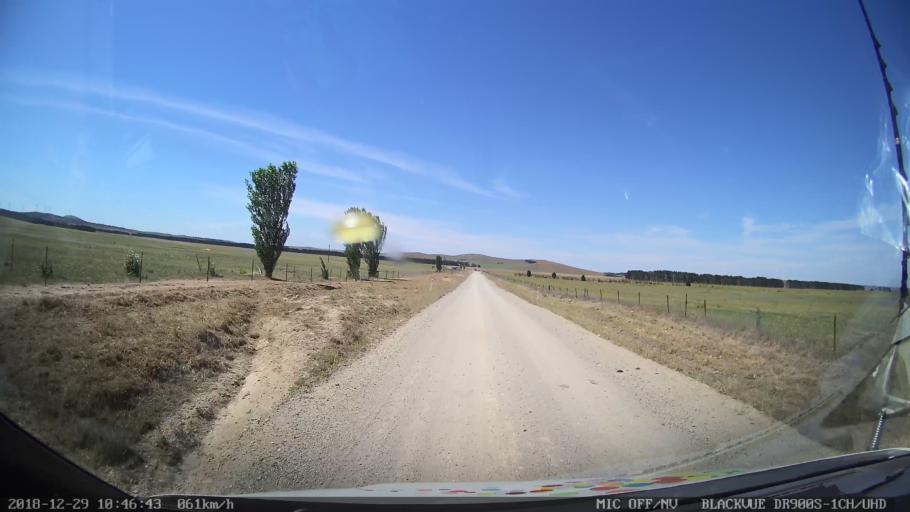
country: AU
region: New South Wales
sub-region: Palerang
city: Bungendore
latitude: -35.0528
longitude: 149.5163
